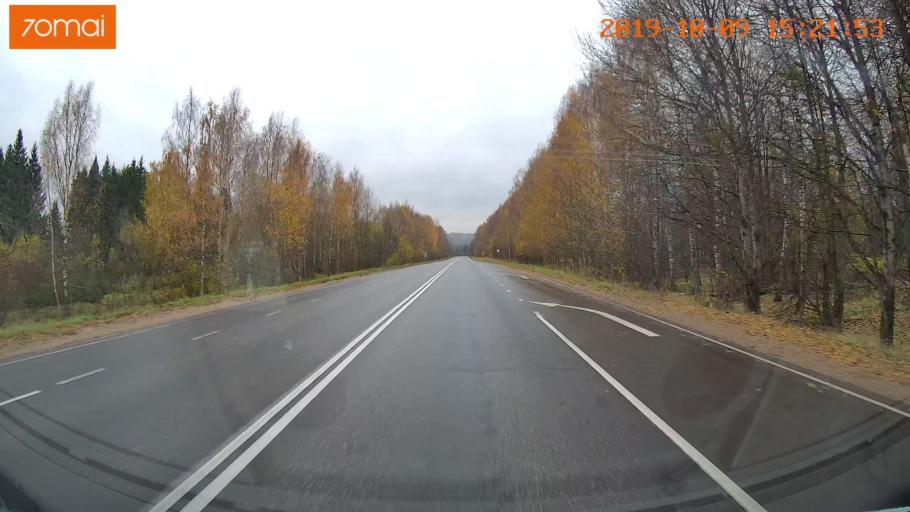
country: RU
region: Kostroma
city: Susanino
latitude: 58.0506
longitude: 41.5090
